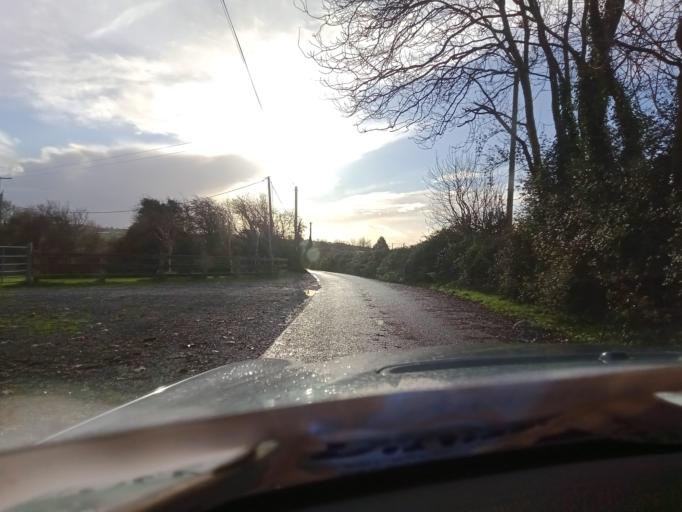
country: IE
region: Leinster
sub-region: Kilkenny
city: Mooncoin
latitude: 52.2756
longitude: -7.1836
